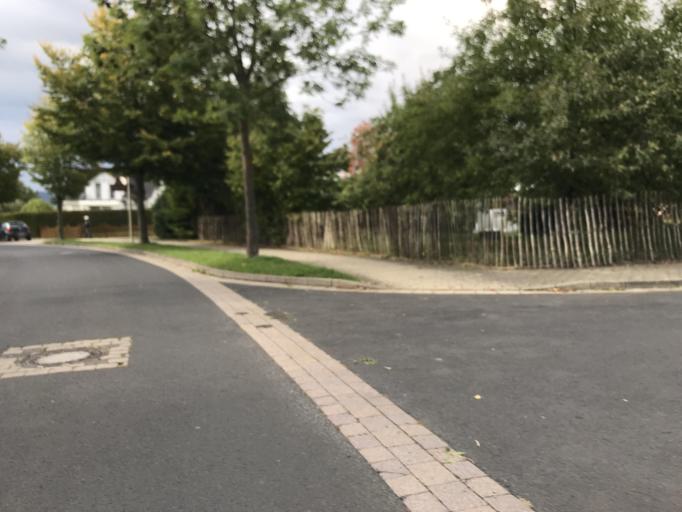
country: DE
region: Hesse
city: Borken
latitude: 51.0402
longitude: 9.2808
